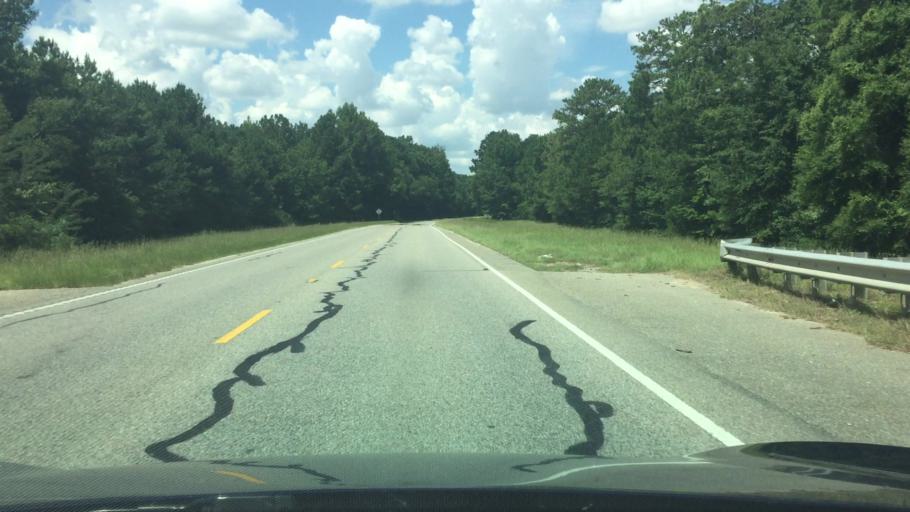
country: US
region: Alabama
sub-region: Montgomery County
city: Pike Road
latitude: 32.3705
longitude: -86.0138
